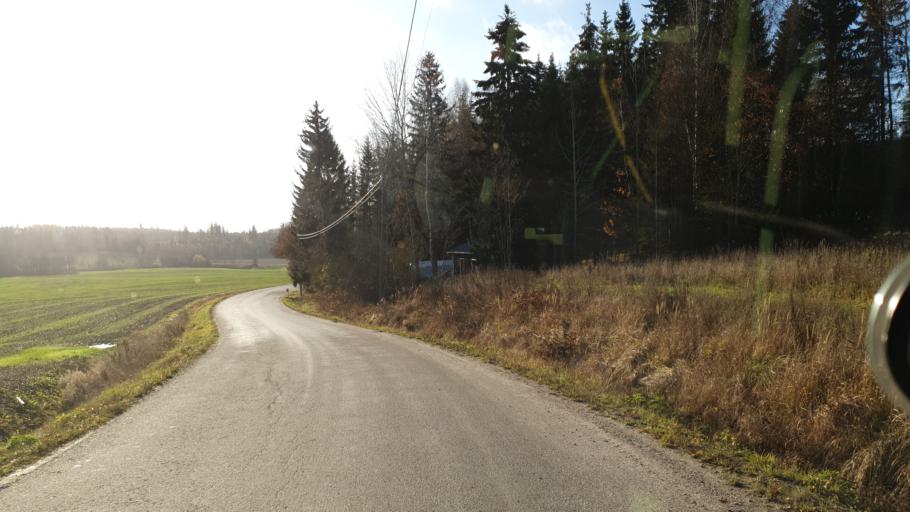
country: FI
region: Uusimaa
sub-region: Helsinki
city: Lohja
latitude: 60.2355
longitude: 24.1685
